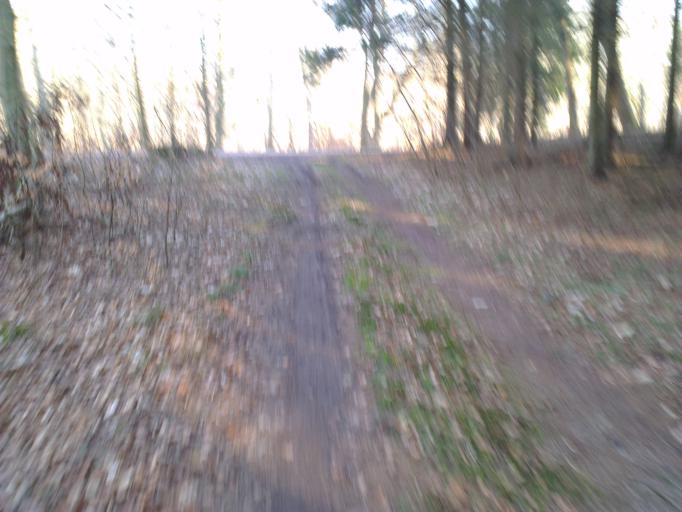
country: DK
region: Capital Region
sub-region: Frederikssund Kommune
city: Jaegerspris
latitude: 55.8924
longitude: 12.0050
